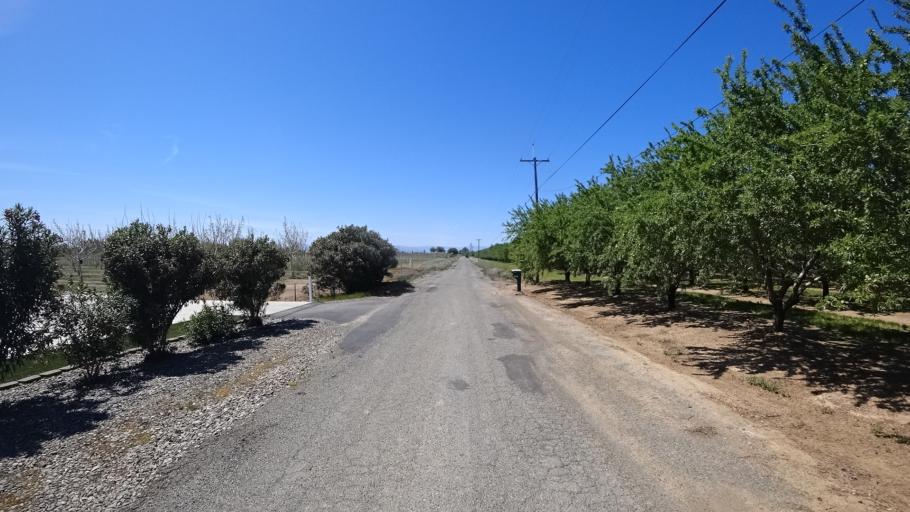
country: US
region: California
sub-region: Glenn County
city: Hamilton City
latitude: 39.7323
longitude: -122.0965
